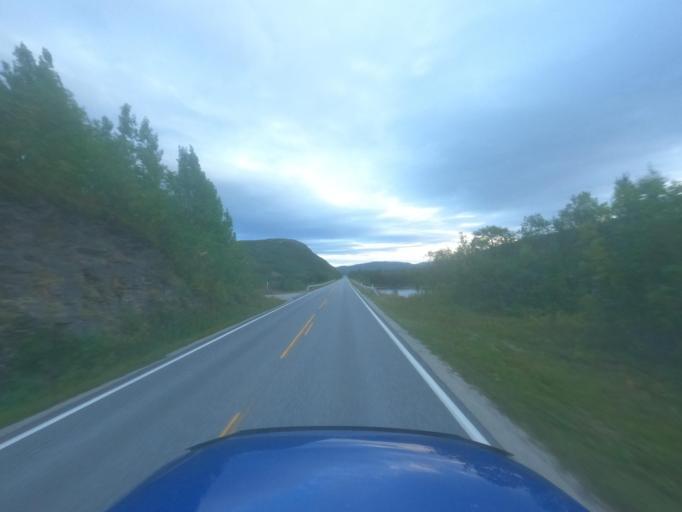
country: NO
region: Finnmark Fylke
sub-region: Porsanger
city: Lakselv
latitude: 69.9264
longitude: 24.9821
